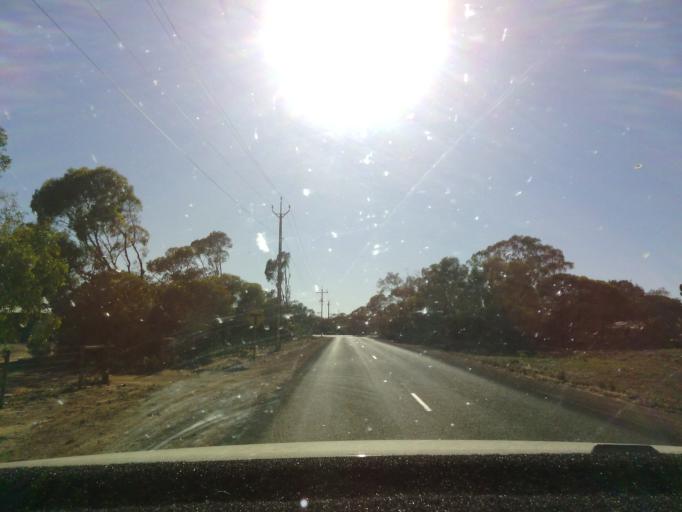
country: AU
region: South Australia
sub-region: Berri and Barmera
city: Monash
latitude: -34.2253
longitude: 140.5725
